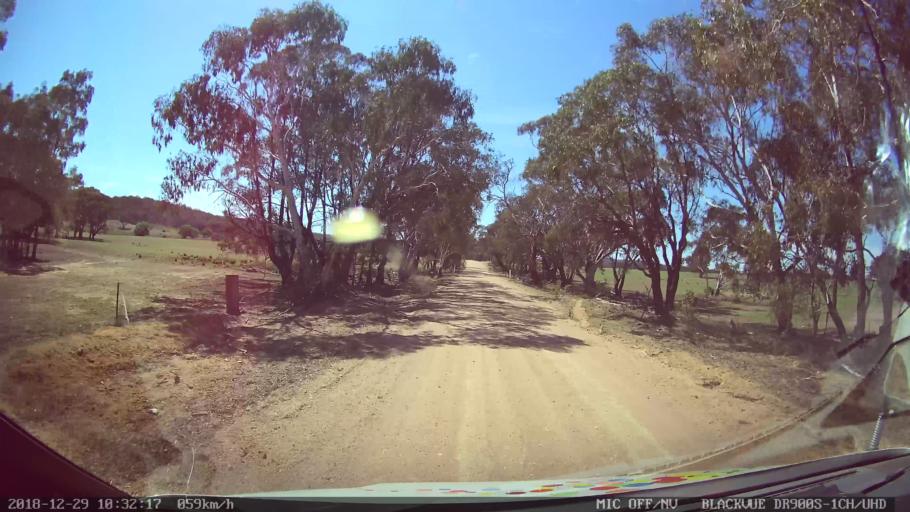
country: AU
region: New South Wales
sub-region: Yass Valley
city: Gundaroo
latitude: -34.9737
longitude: 149.4632
